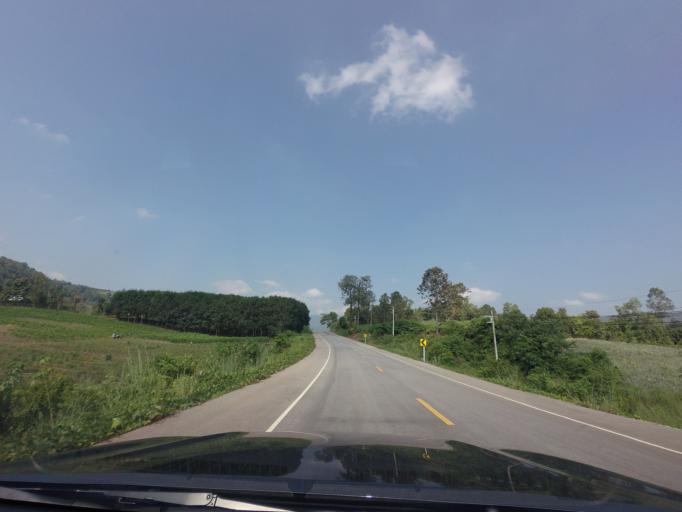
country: TH
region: Loei
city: Na Haeo
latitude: 17.4965
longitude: 101.0246
